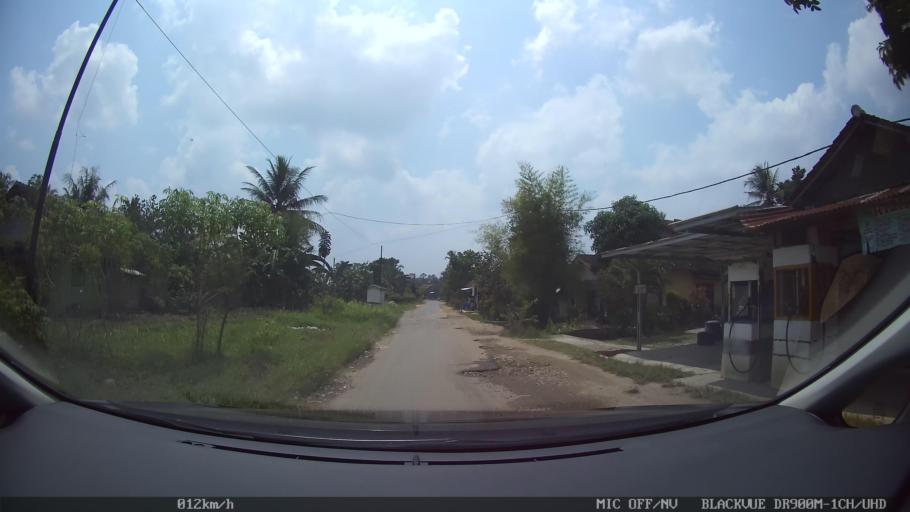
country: ID
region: Lampung
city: Pringsewu
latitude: -5.3401
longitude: 104.9820
